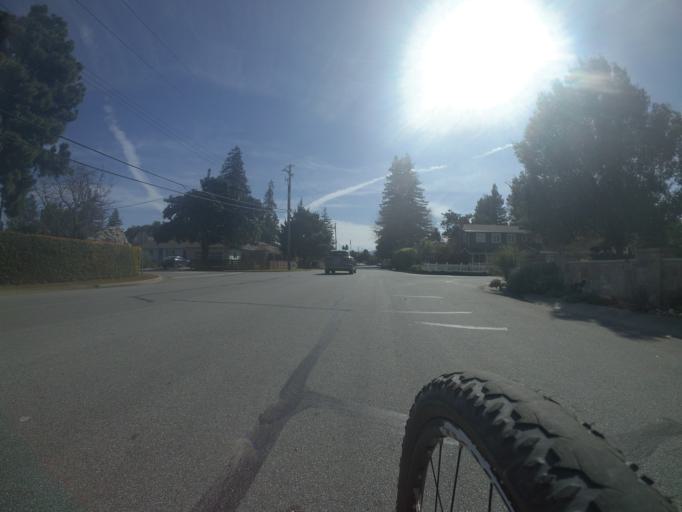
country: US
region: California
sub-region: Santa Clara County
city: Sunnyvale
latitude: 37.3512
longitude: -122.0659
